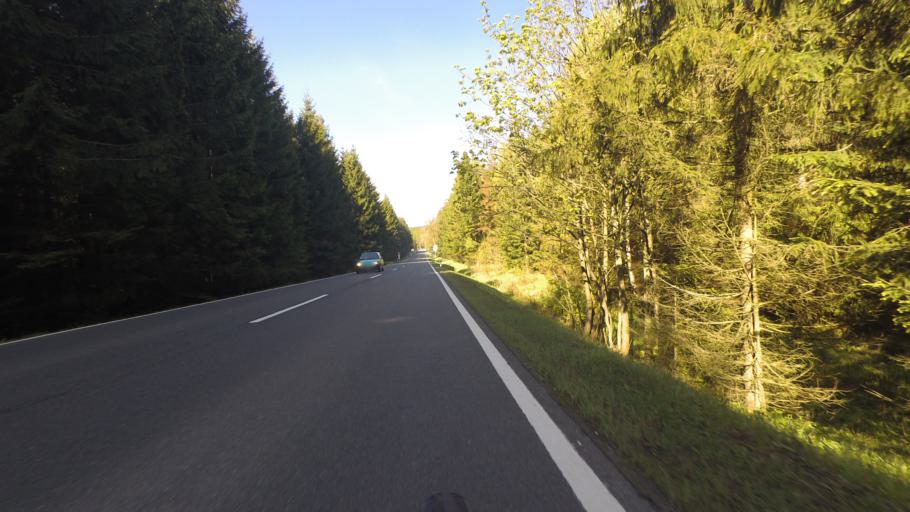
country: DE
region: Saxony-Anhalt
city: Elbingerode
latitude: 51.7823
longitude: 10.7419
